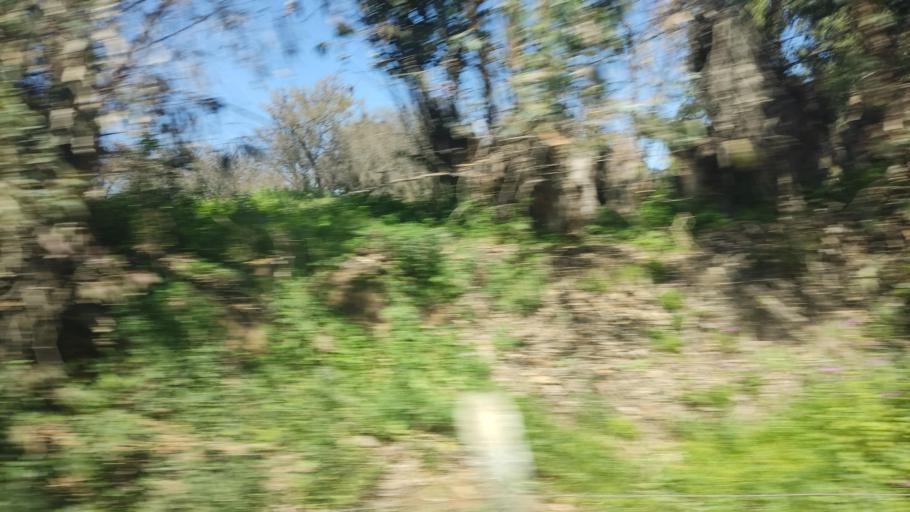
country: CL
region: Valparaiso
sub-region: Provincia de Marga Marga
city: Villa Alemana
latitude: -33.1513
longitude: -71.3376
